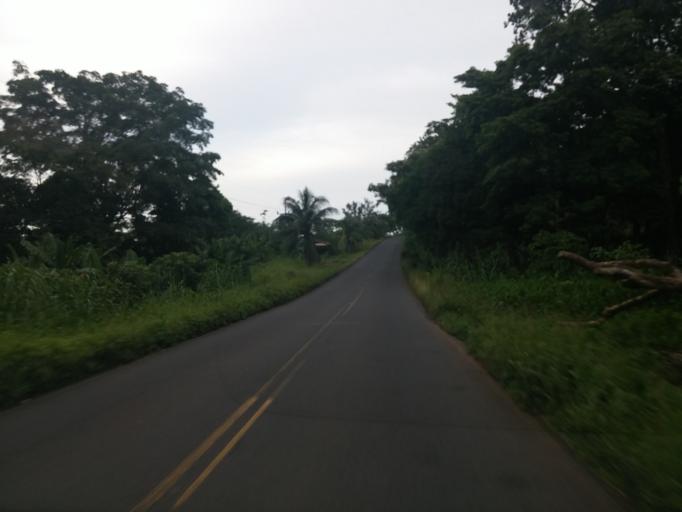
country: CR
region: Alajuela
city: Bijagua
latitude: 10.8099
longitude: -85.0196
